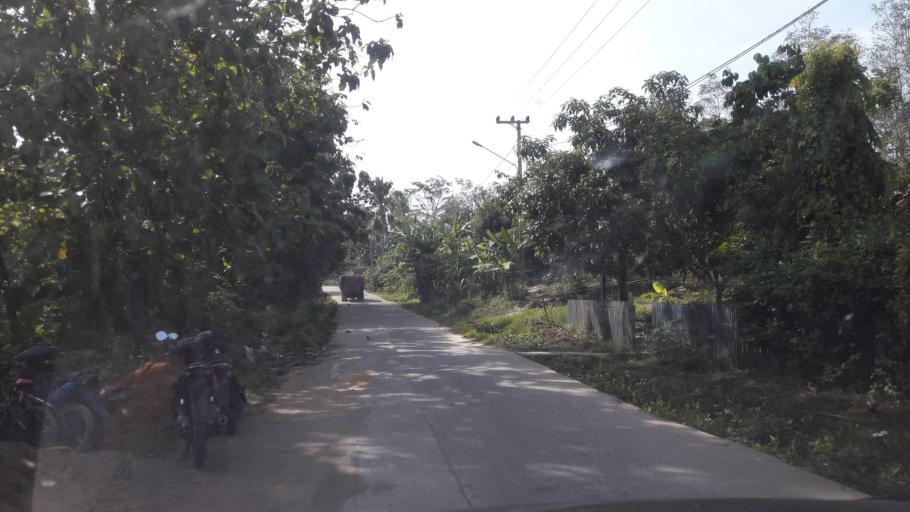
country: ID
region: South Sumatra
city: Gunungmenang
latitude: -3.3323
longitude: 104.0413
